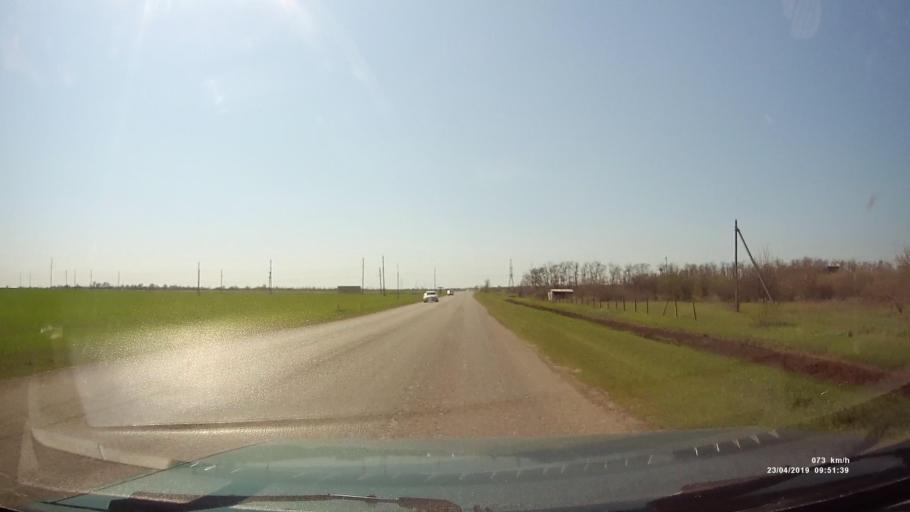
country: RU
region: Rostov
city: Orlovskiy
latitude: 46.8533
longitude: 42.0424
